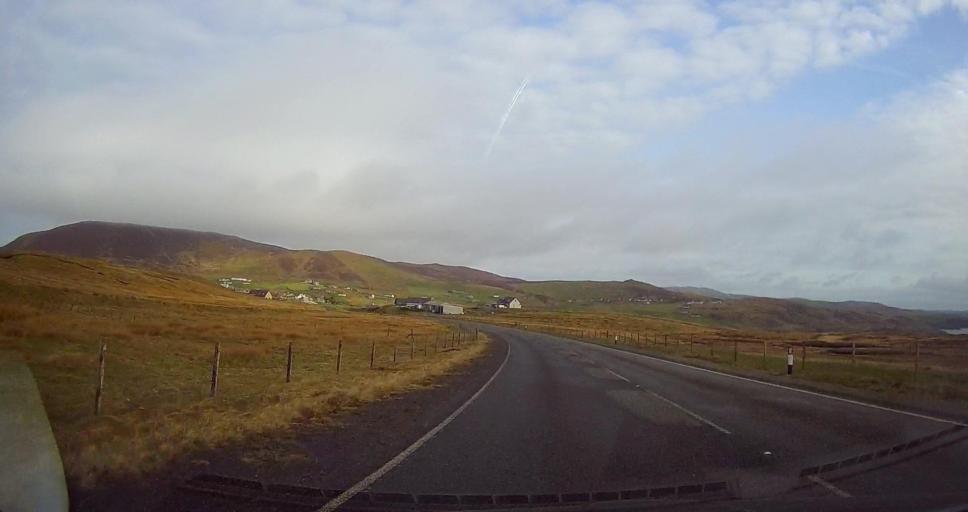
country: GB
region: Scotland
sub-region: Shetland Islands
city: Sandwick
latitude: 60.0906
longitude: -1.2285
